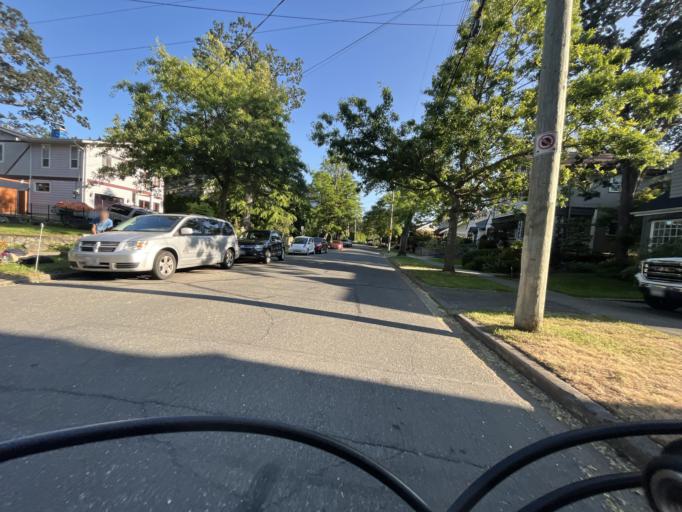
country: CA
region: British Columbia
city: Victoria
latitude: 48.4225
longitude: -123.3450
